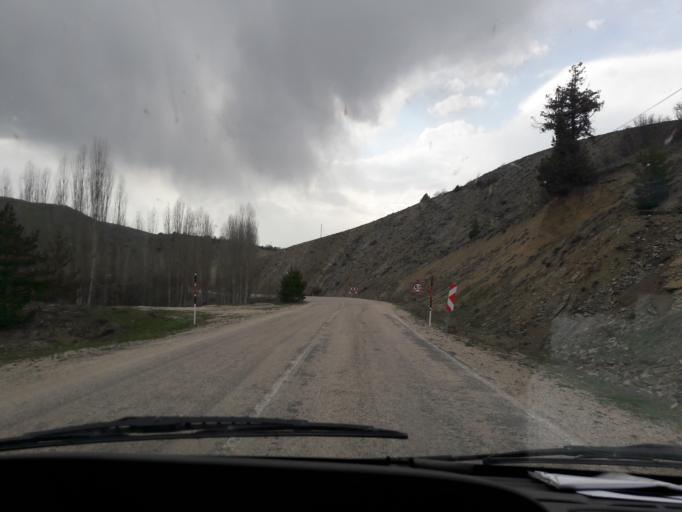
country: TR
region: Giresun
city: Alucra
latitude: 40.2909
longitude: 38.8121
